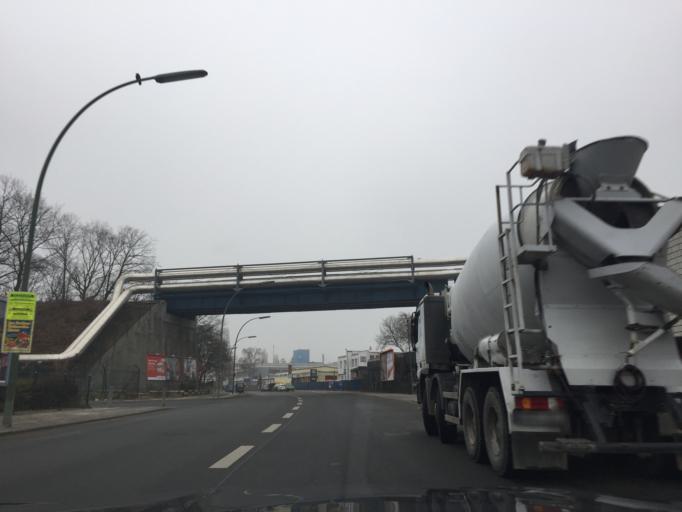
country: DE
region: Berlin
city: Haselhorst
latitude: 52.5285
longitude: 13.2393
